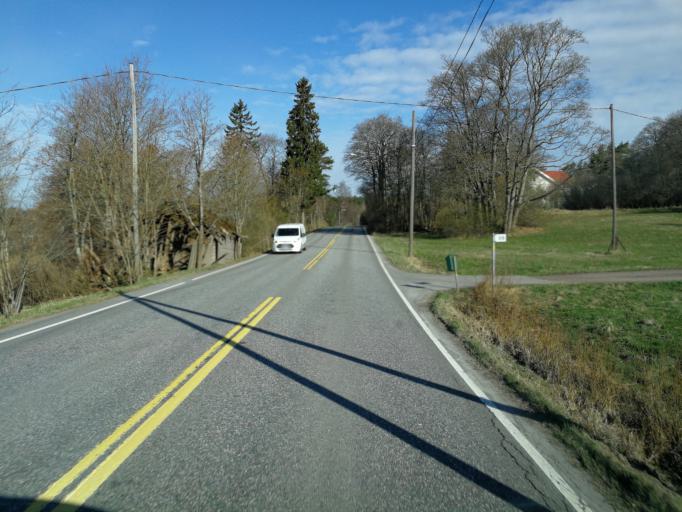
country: FI
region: Uusimaa
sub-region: Helsinki
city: Kirkkonummi
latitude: 60.2206
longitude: 24.4710
